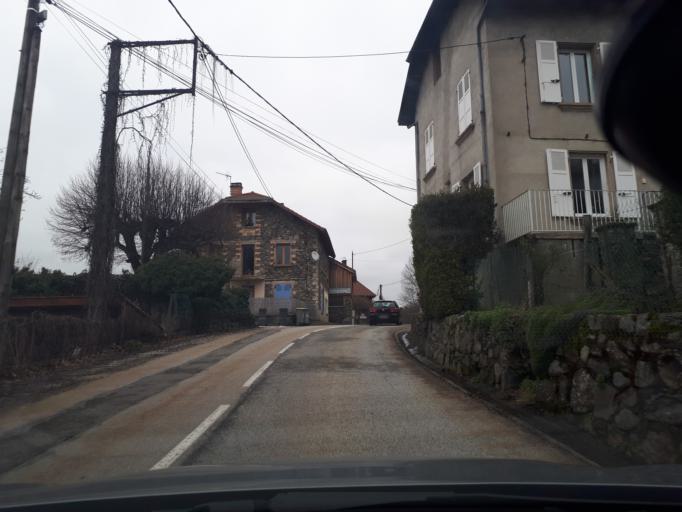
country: FR
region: Rhone-Alpes
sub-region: Departement de l'Isere
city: Vaulnaveys-le-Bas
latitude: 45.1147
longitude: 5.8308
